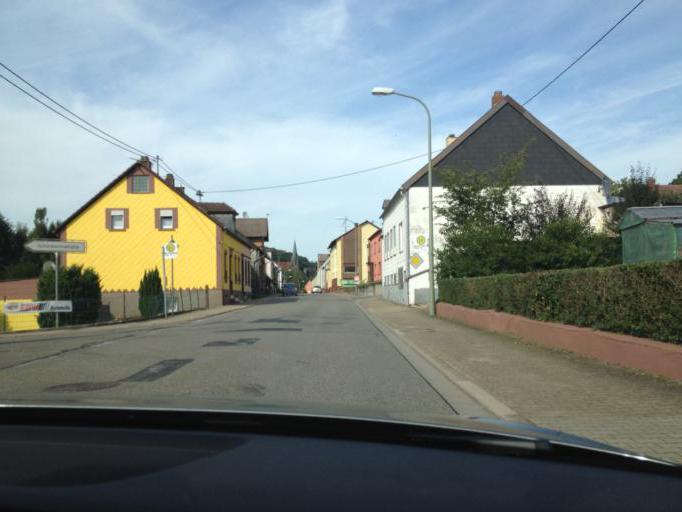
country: DE
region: Rheinland-Pfalz
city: Breitenbach
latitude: 49.4300
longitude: 7.2662
